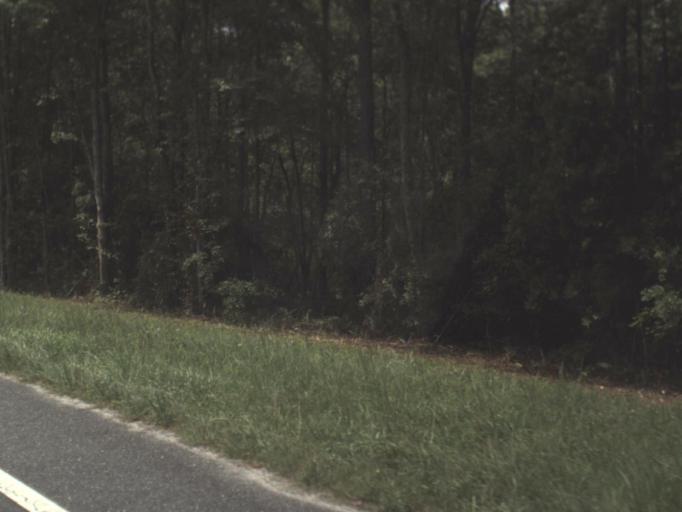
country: US
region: Georgia
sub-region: Echols County
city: Statenville
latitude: 30.6193
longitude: -83.1162
